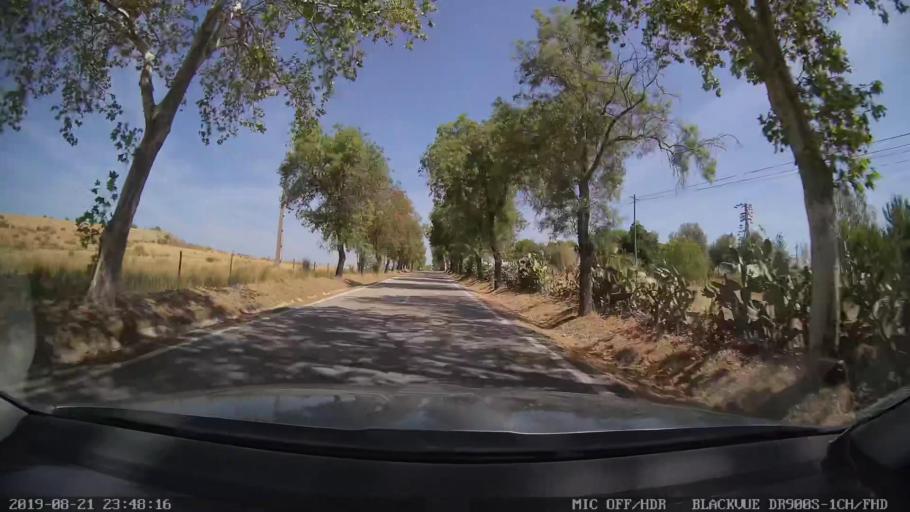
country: PT
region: Castelo Branco
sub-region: Idanha-A-Nova
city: Idanha-a-Nova
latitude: 39.8627
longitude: -7.2581
